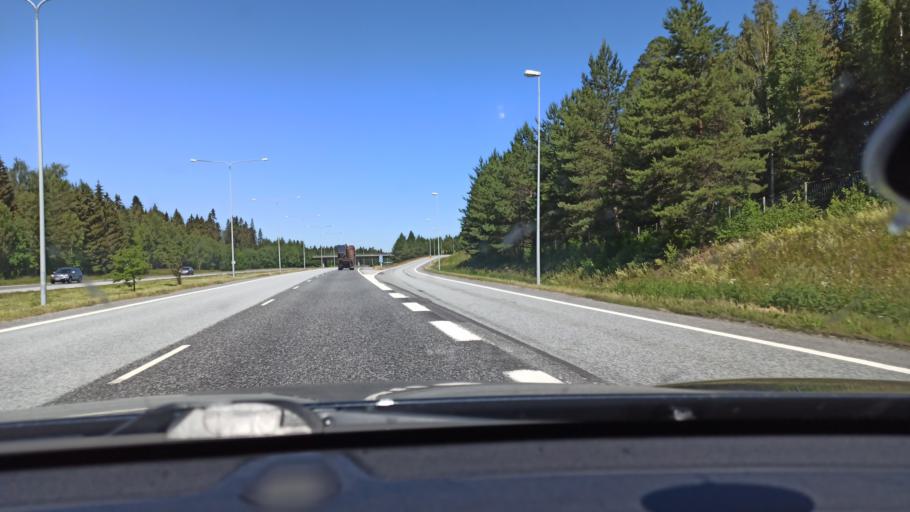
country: FI
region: Ostrobothnia
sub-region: Vaasa
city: Ristinummi
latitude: 63.0505
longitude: 21.7179
